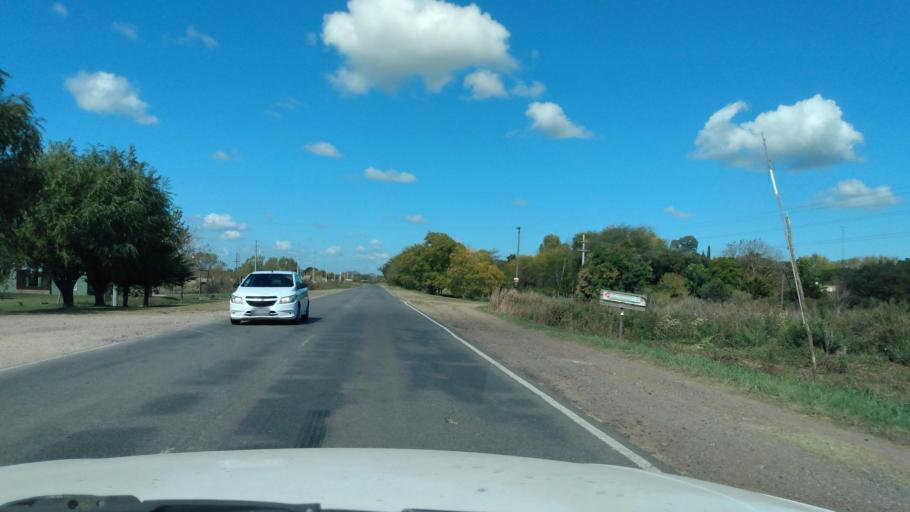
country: AR
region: Buenos Aires
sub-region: Partido de Mercedes
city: Mercedes
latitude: -34.6963
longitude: -59.4038
